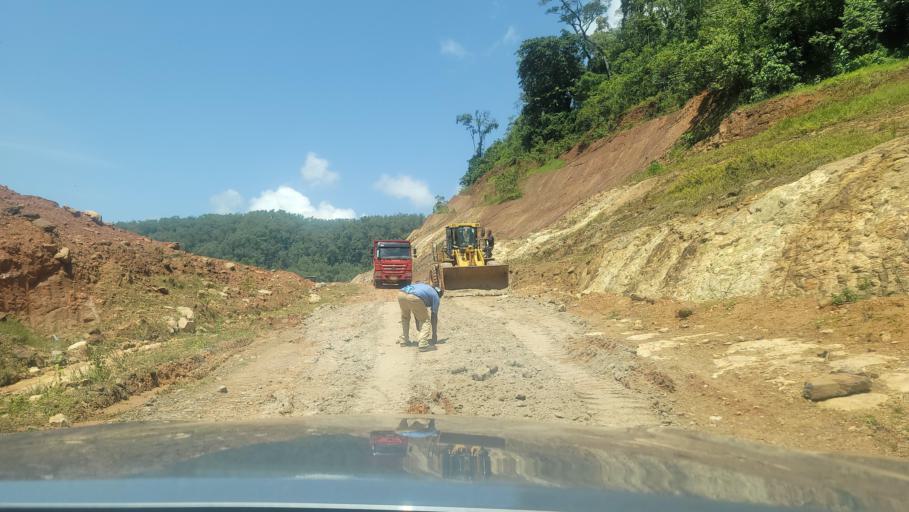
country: ET
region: Southern Nations, Nationalities, and People's Region
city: Bonga
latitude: 7.6122
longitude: 36.1998
